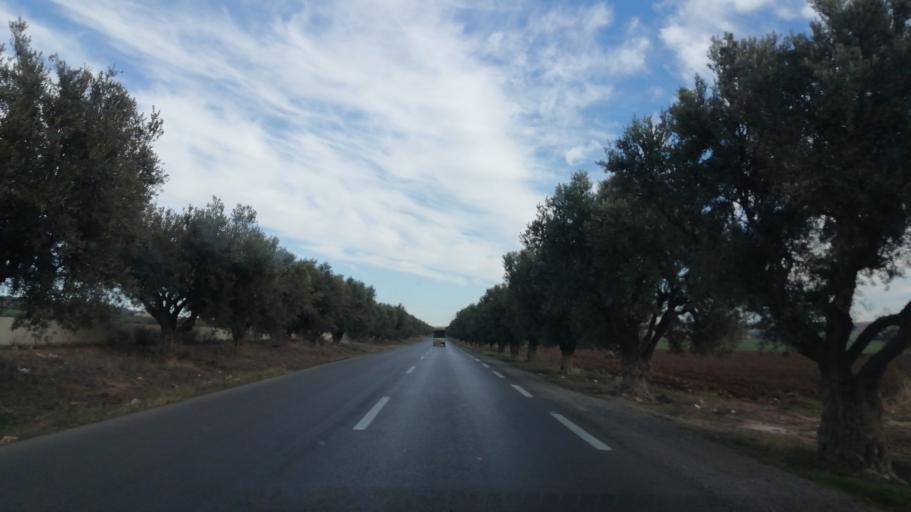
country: DZ
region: Sidi Bel Abbes
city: Sidi Bel Abbes
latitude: 35.1782
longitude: -0.4350
